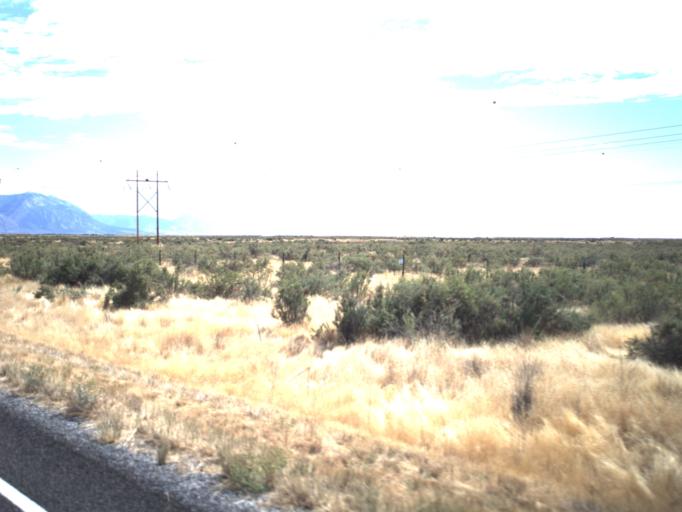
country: US
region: Utah
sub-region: Box Elder County
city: Tremonton
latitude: 41.5979
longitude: -112.2957
